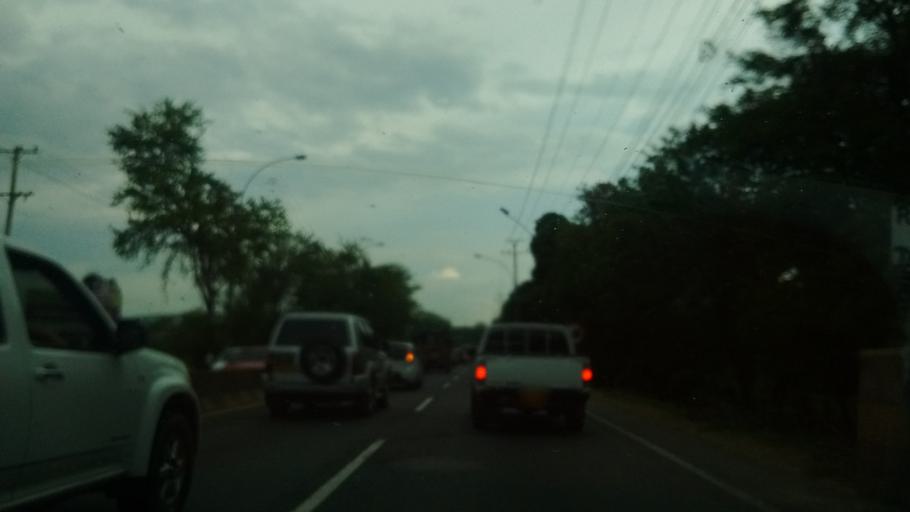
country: CO
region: Valle del Cauca
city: Cali
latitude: 3.3564
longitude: -76.5237
